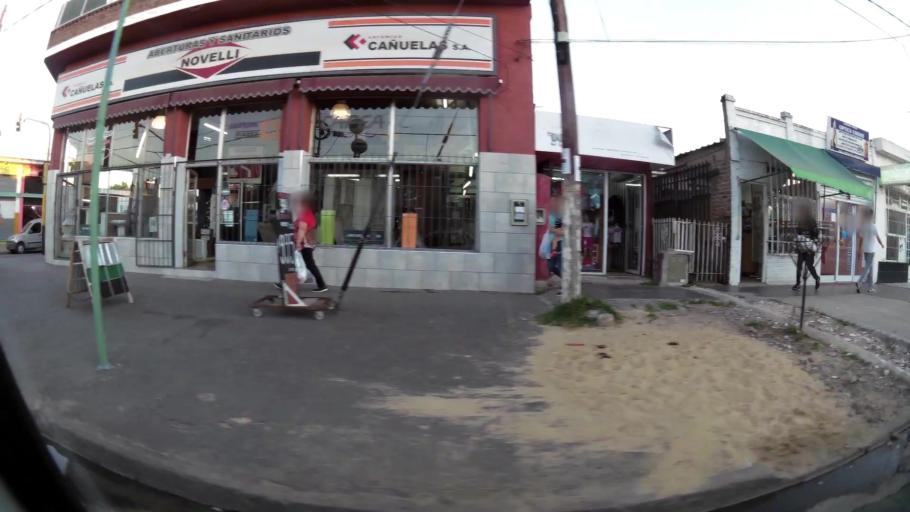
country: AR
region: Buenos Aires
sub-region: Partido de Quilmes
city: Quilmes
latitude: -34.8101
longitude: -58.1876
